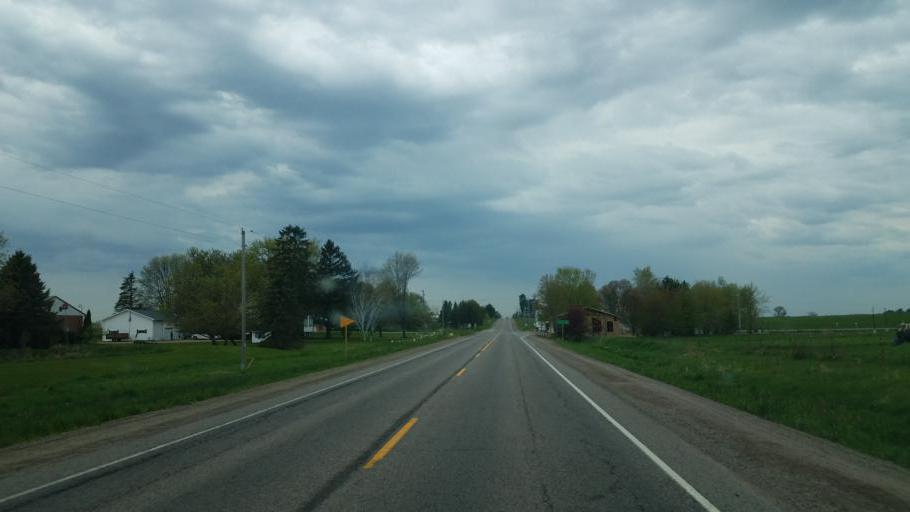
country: US
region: Wisconsin
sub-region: Marathon County
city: Spencer
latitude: 44.5982
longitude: -90.3533
